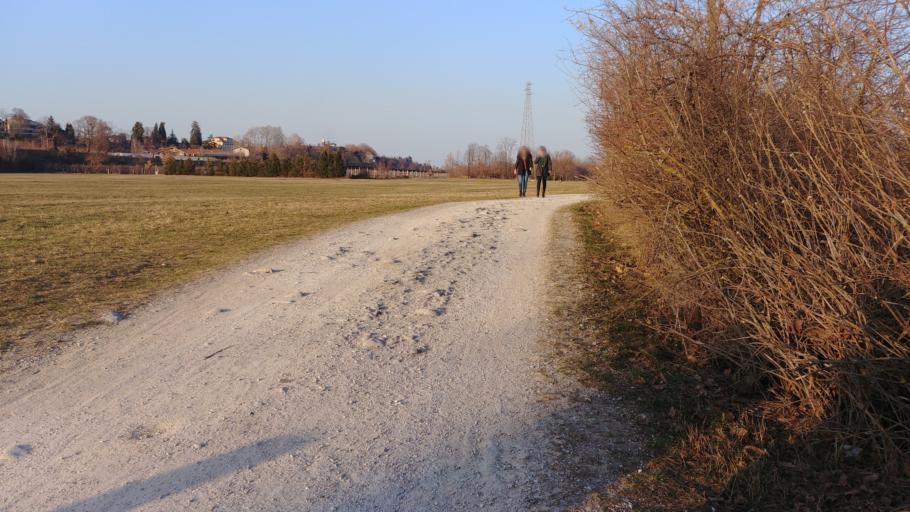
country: IT
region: Piedmont
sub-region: Provincia di Cuneo
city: Boves
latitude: 44.3573
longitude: 7.5327
